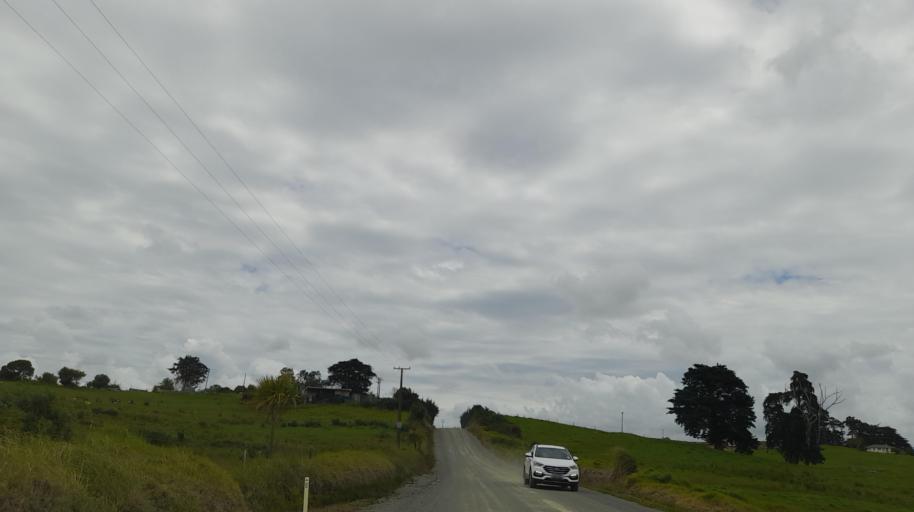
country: NZ
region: Auckland
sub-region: Auckland
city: Wellsford
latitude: -36.2624
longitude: 174.4125
